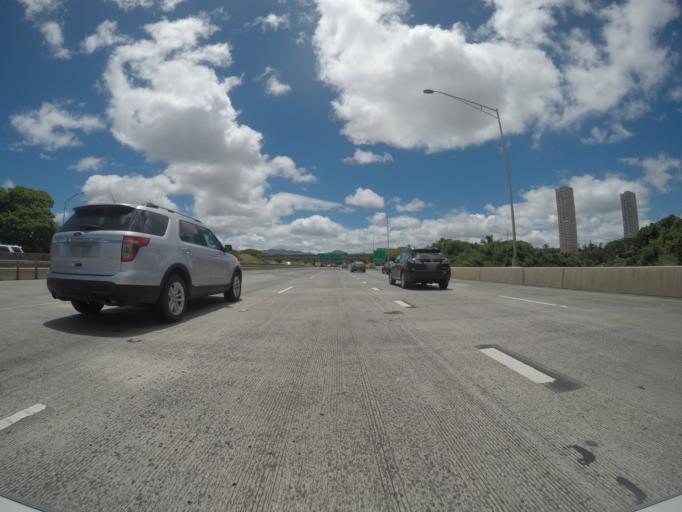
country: US
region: Hawaii
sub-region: Honolulu County
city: Pearl City, Manana
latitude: 21.3933
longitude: -157.9780
